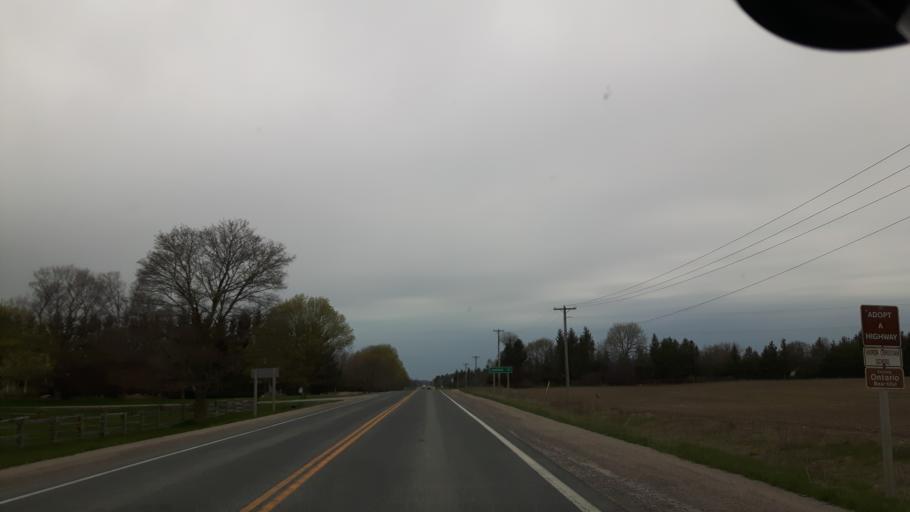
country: CA
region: Ontario
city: Bluewater
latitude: 43.6221
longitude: -81.5512
